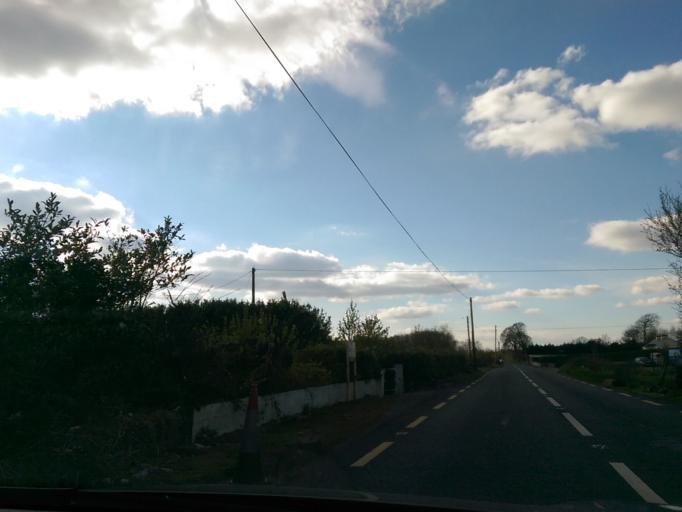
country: IE
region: Connaught
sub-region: County Galway
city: Loughrea
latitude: 53.2069
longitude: -8.4771
